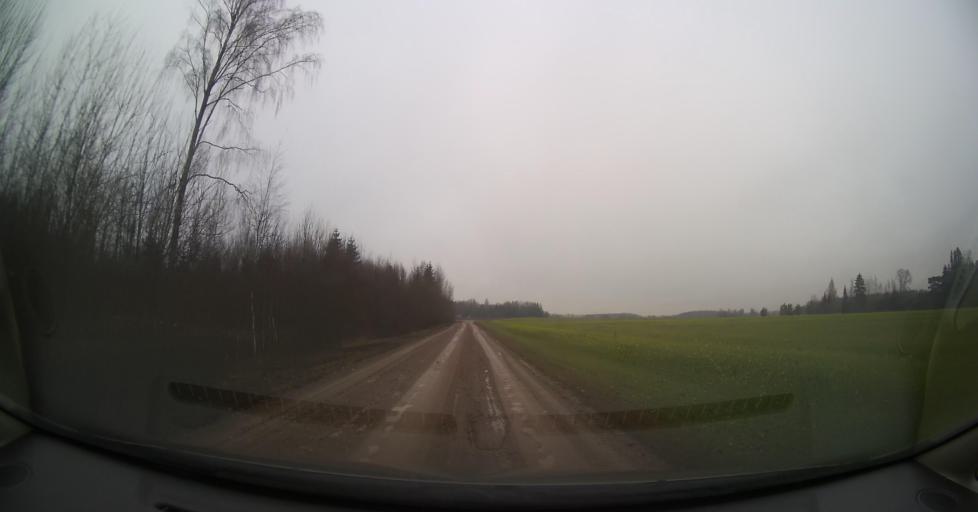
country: EE
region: Tartu
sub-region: Tartu linn
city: Tartu
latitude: 58.3954
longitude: 26.9234
